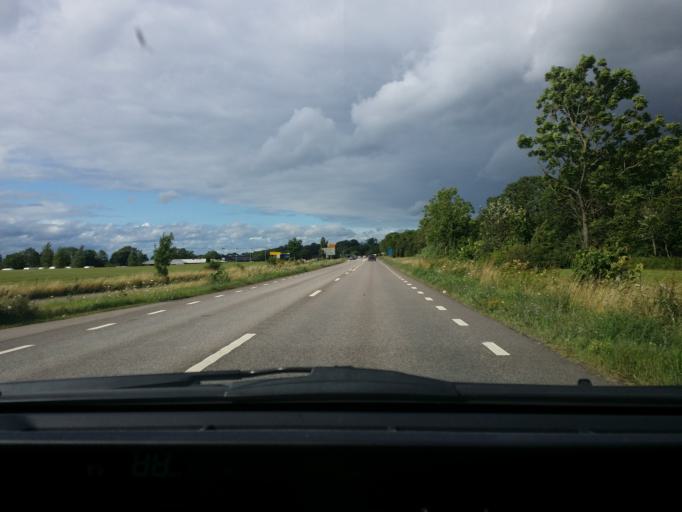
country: SE
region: Kalmar
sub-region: Borgholms Kommun
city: Borgholm
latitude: 56.9022
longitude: 16.7335
